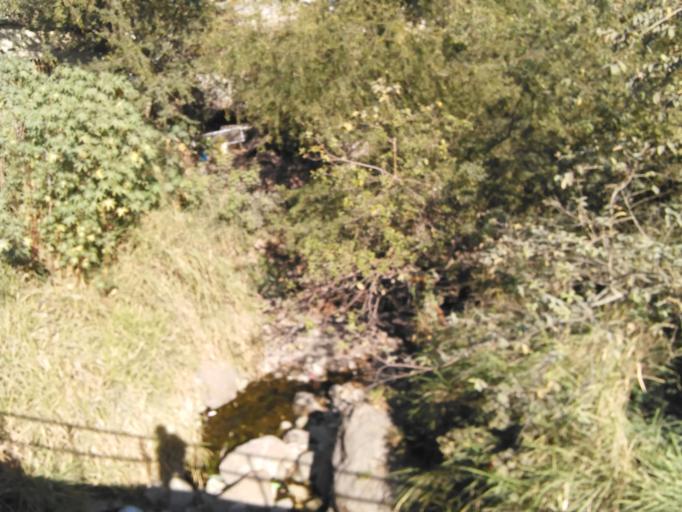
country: MX
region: Nayarit
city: Tepic
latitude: 21.5292
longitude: -104.8938
